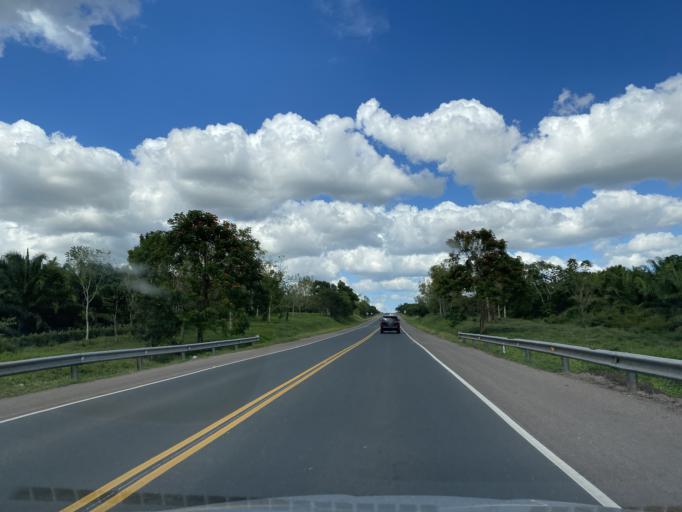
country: DO
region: Monte Plata
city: Monte Plata
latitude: 18.7225
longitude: -69.7605
